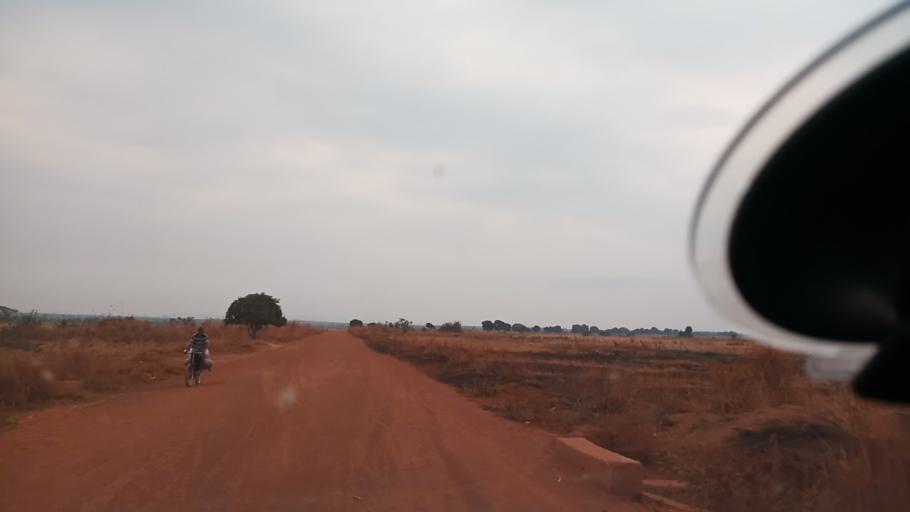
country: ZM
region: Luapula
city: Nchelenge
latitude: -9.2762
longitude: 28.3191
